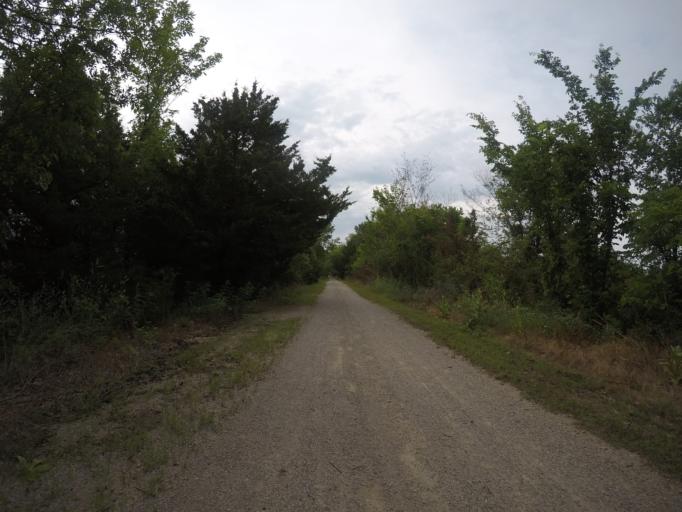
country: US
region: Kansas
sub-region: Franklin County
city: Ottawa
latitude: 38.4737
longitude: -95.2741
